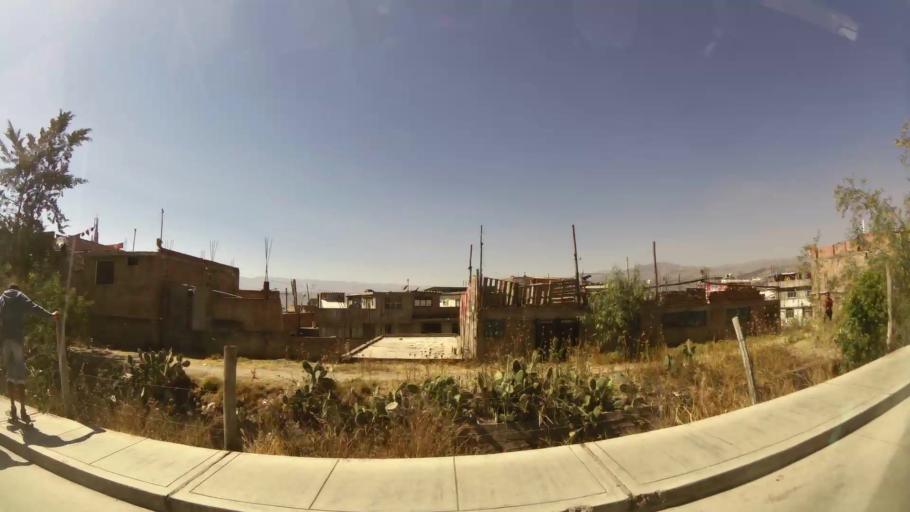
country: PE
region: Ayacucho
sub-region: Provincia de Huamanga
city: Ayacucho
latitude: -13.1516
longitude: -74.2308
